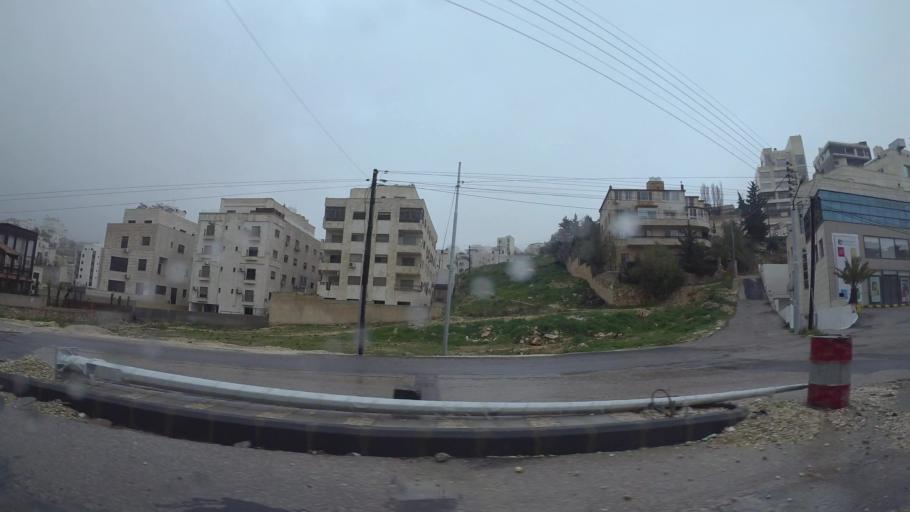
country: JO
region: Amman
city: Al Jubayhah
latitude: 32.0115
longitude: 35.8327
